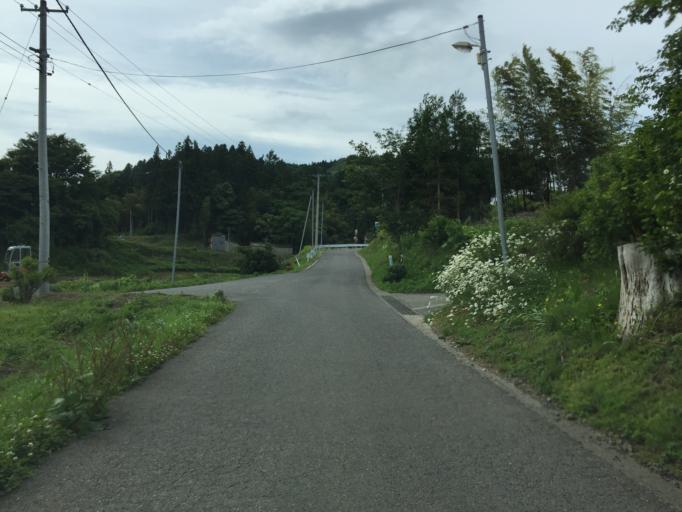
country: JP
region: Fukushima
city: Funehikimachi-funehiki
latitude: 37.4599
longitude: 140.6389
